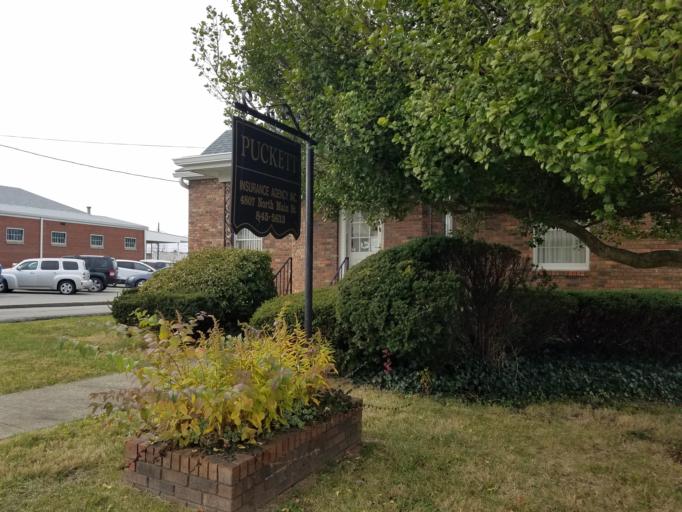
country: US
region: Kentucky
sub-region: Henry County
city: Eminence
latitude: 38.3715
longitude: -85.1798
